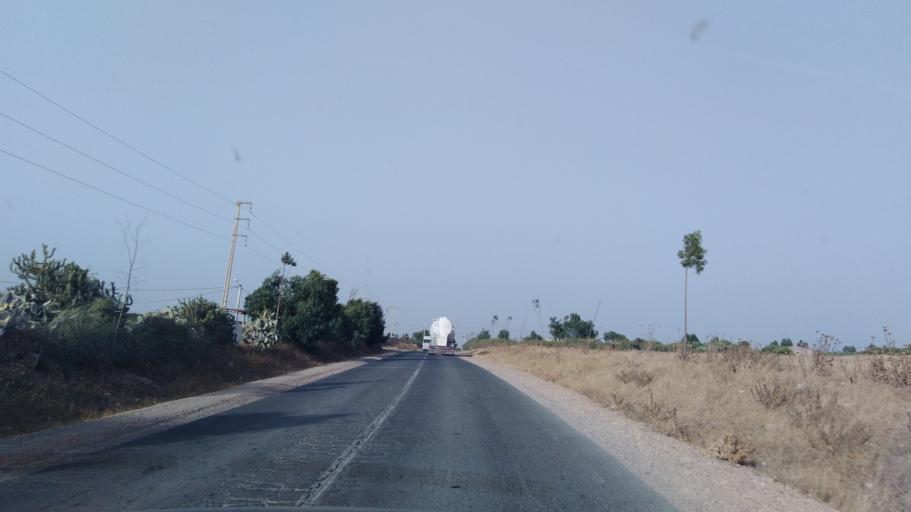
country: MA
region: Chaouia-Ouardigha
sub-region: Settat Province
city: Settat
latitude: 33.0795
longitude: -7.5858
